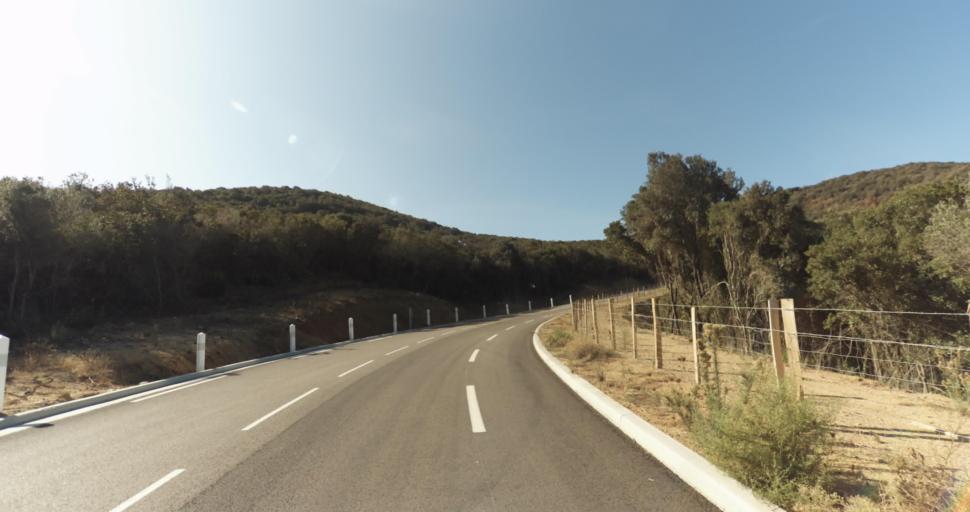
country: FR
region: Corsica
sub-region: Departement de la Corse-du-Sud
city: Ajaccio
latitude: 41.9265
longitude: 8.6491
